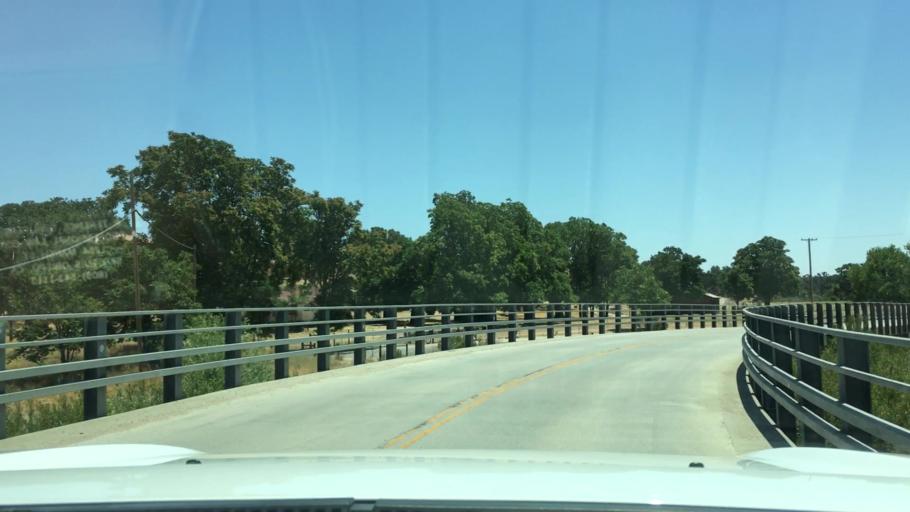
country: US
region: California
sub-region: San Luis Obispo County
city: Paso Robles
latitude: 35.6011
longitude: -120.6034
